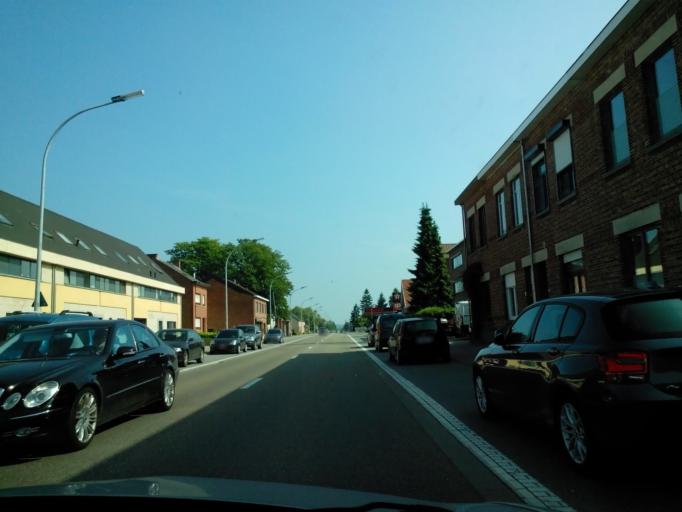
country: BE
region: Flanders
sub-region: Provincie Vlaams-Brabant
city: Leuven
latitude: 50.9123
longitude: 4.7146
